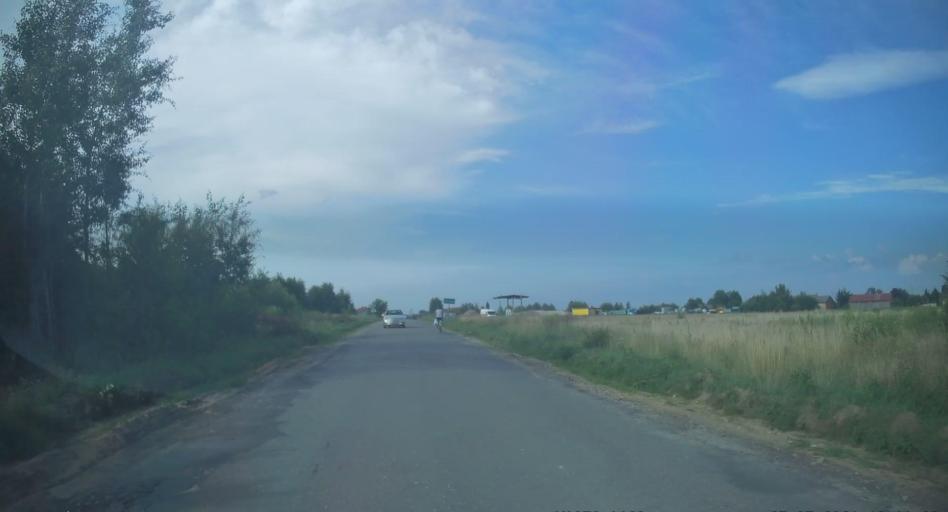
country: PL
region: Swietokrzyskie
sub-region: Powiat konecki
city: Gowarczow
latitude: 51.2703
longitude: 20.3693
